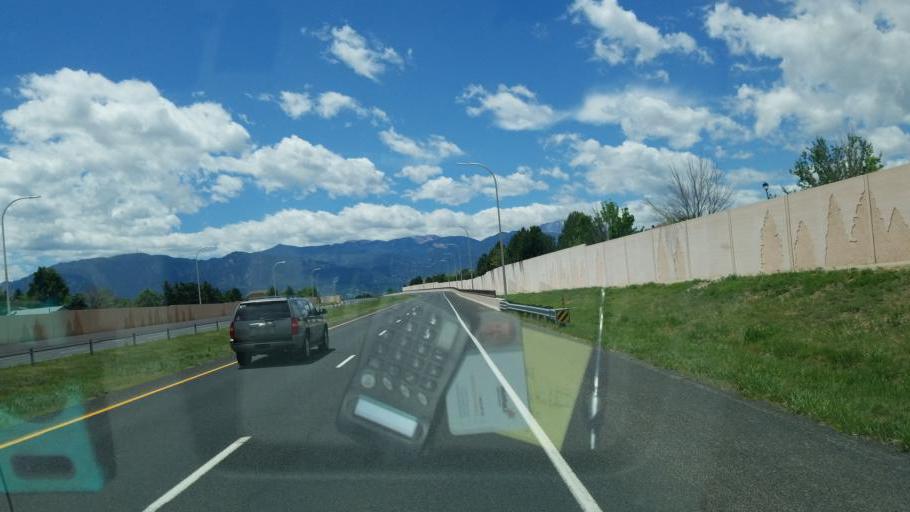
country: US
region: Colorado
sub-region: El Paso County
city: Security-Widefield
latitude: 38.7816
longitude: -104.7276
